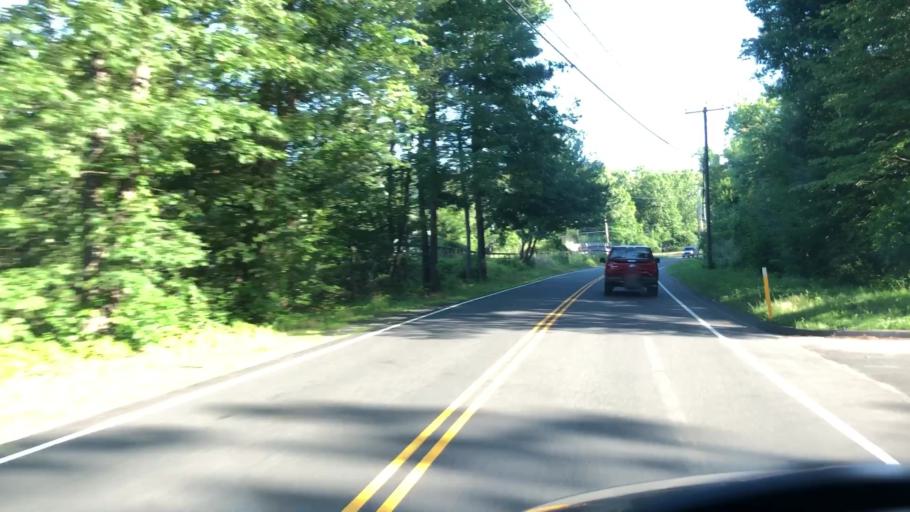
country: US
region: Massachusetts
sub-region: Hampshire County
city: Easthampton
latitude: 42.2825
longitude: -72.6540
